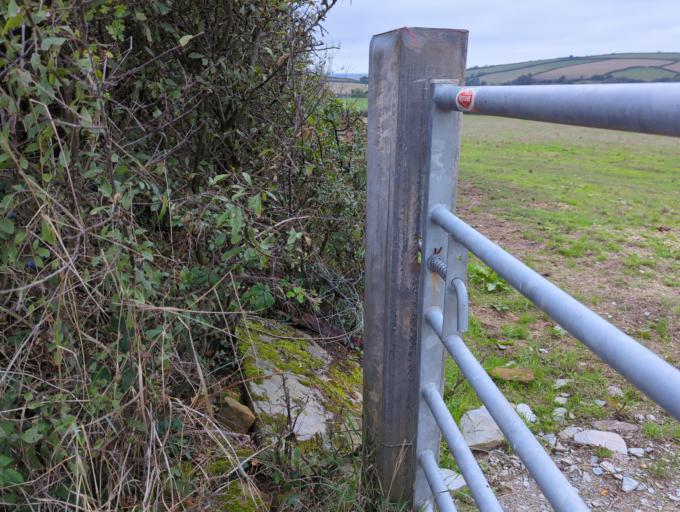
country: GB
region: England
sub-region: Cornwall
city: Wadebridge
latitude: 50.5695
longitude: -4.7977
